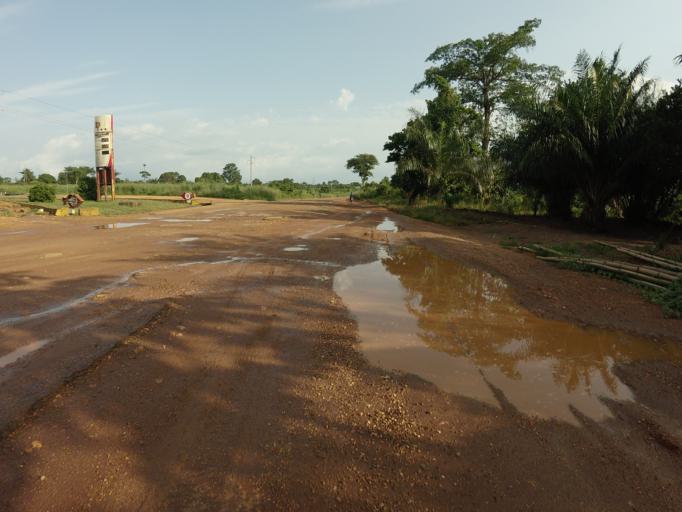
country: GH
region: Volta
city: Hohoe
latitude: 7.0886
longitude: 0.4450
